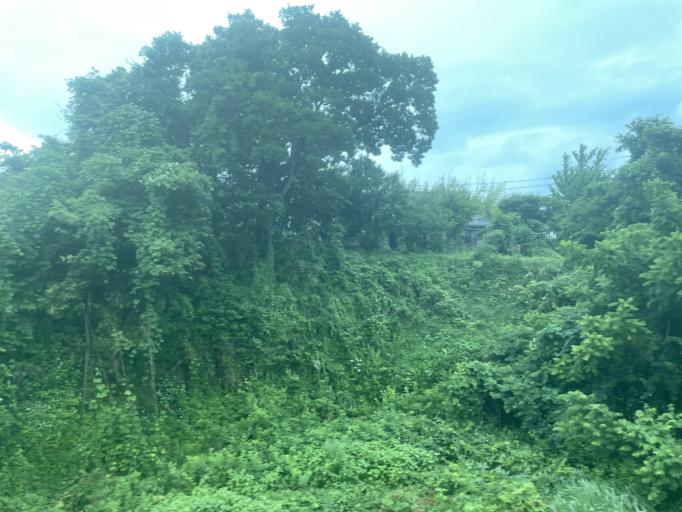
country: JP
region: Niigata
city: Kashiwazaki
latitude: 37.3602
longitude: 138.5261
